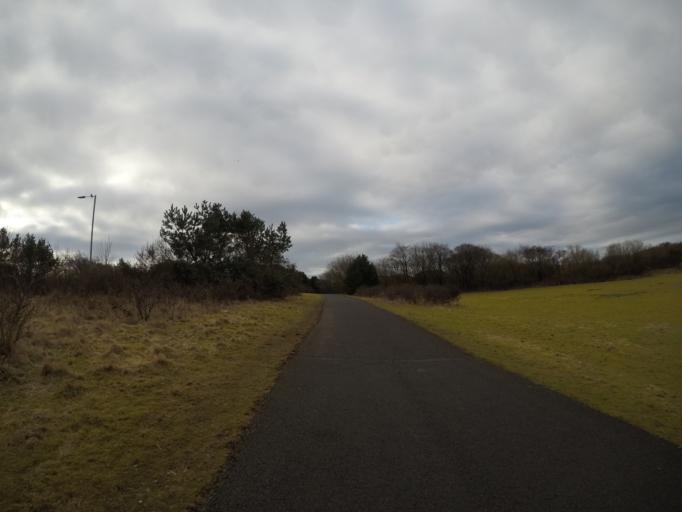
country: GB
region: Scotland
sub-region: North Ayrshire
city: Irvine
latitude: 55.6039
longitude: -4.6807
